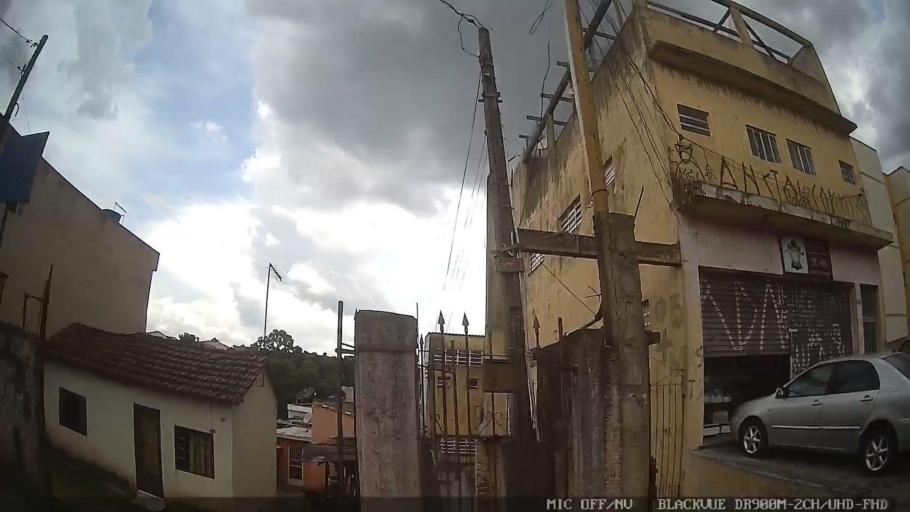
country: BR
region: Sao Paulo
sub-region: Ferraz De Vasconcelos
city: Ferraz de Vasconcelos
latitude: -23.5448
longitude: -46.3639
